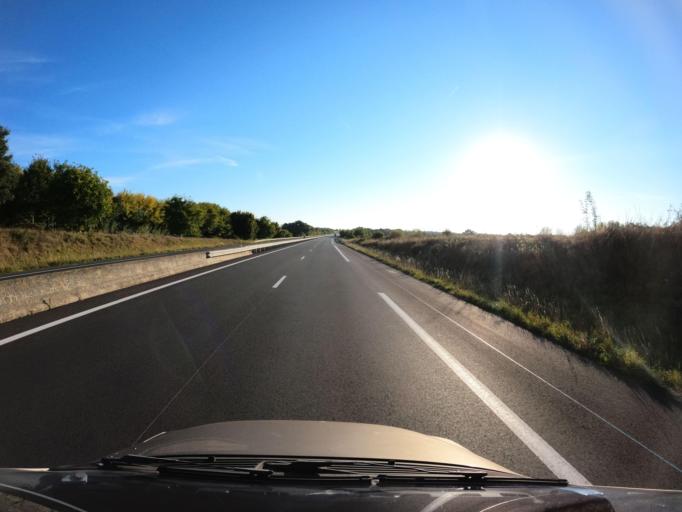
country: FR
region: Pays de la Loire
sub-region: Departement de la Vendee
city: Saint-Fulgent
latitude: 46.8414
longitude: -1.1522
